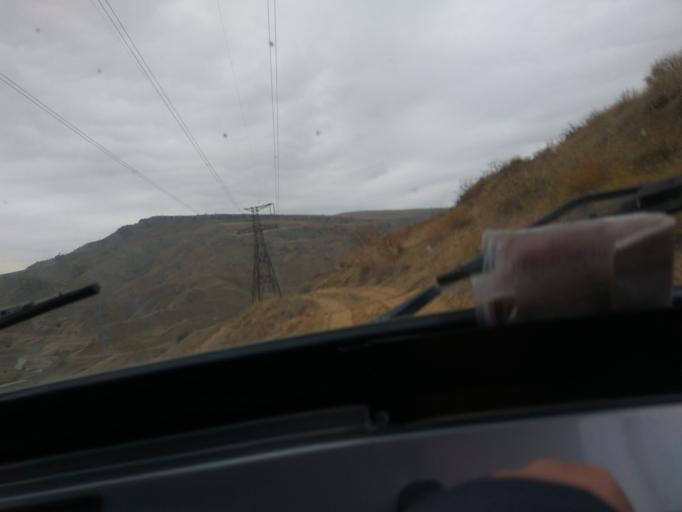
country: RU
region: Dagestan
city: Korkmaskala
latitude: 43.0029
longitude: 47.2163
